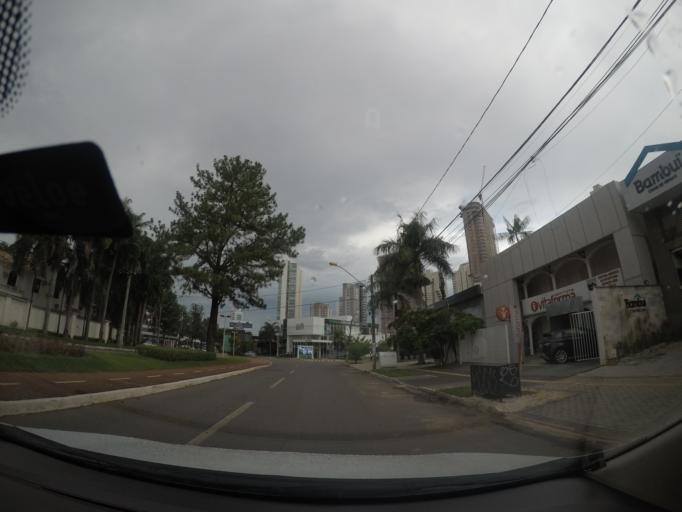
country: BR
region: Goias
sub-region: Goiania
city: Goiania
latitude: -16.7022
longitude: -49.2574
